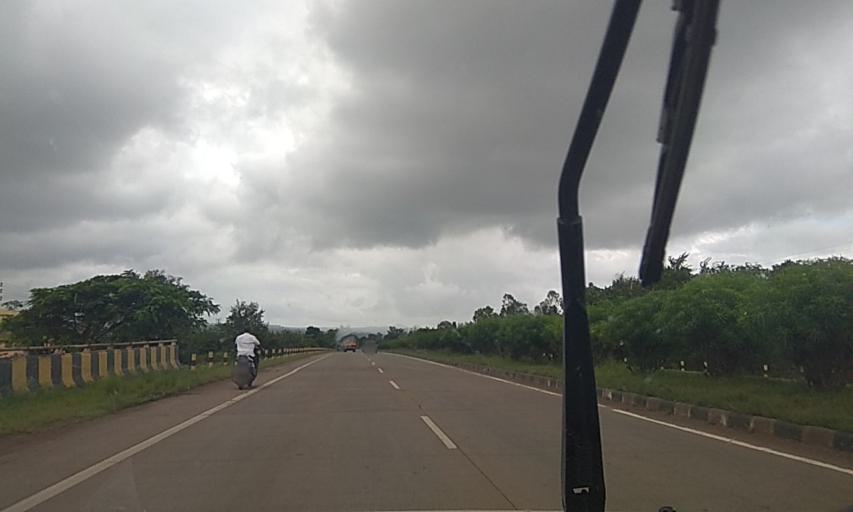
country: IN
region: Karnataka
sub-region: Belgaum
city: Sankeshwar
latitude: 16.2754
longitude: 74.4548
